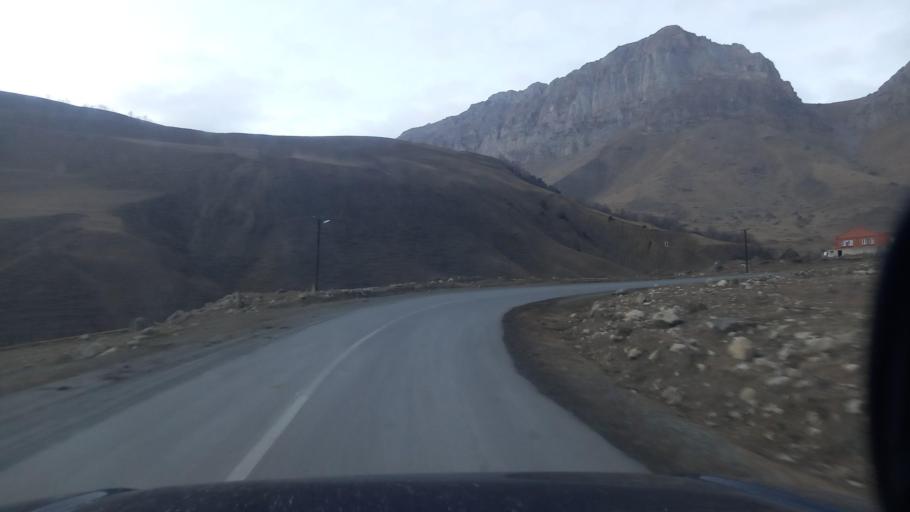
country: RU
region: Ingushetiya
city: Dzhayrakh
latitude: 42.8180
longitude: 44.8150
